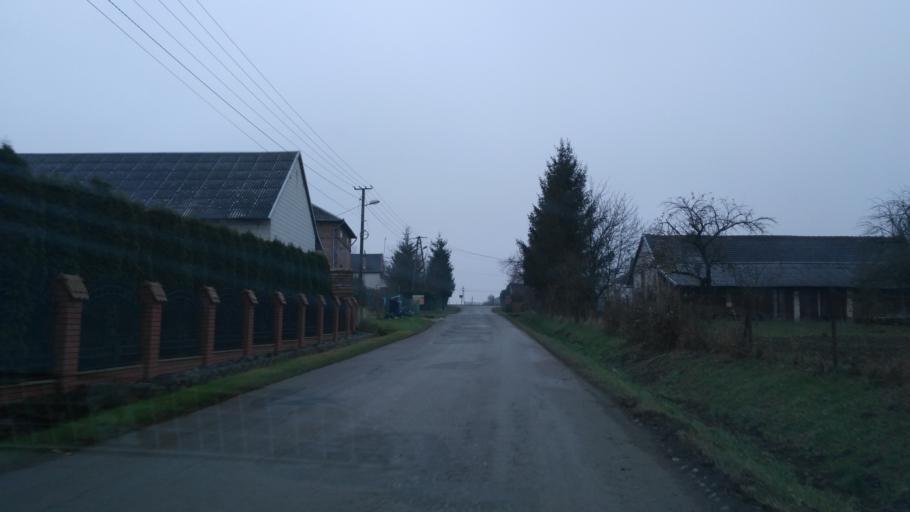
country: PL
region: Subcarpathian Voivodeship
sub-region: Powiat przeworski
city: Zarzecze
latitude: 49.9728
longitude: 22.5550
